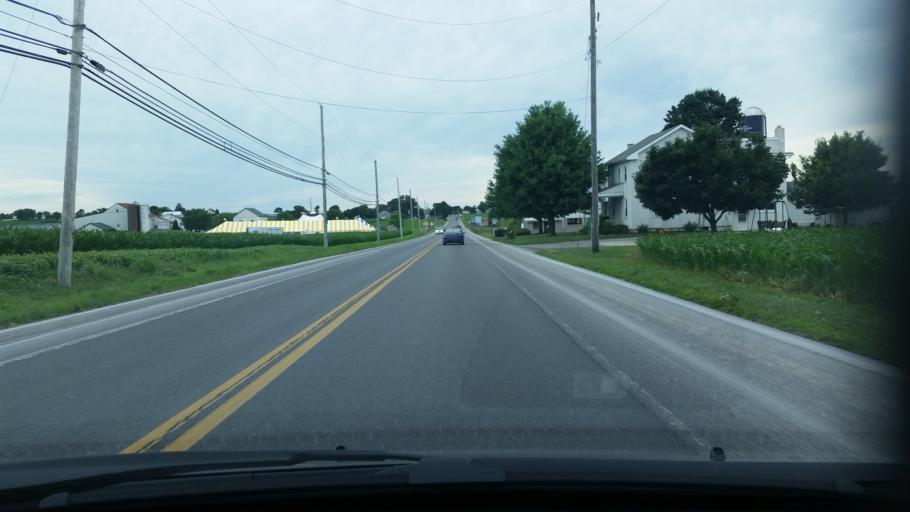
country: US
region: Pennsylvania
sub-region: Lancaster County
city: Intercourse
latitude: 40.0400
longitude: -76.1242
